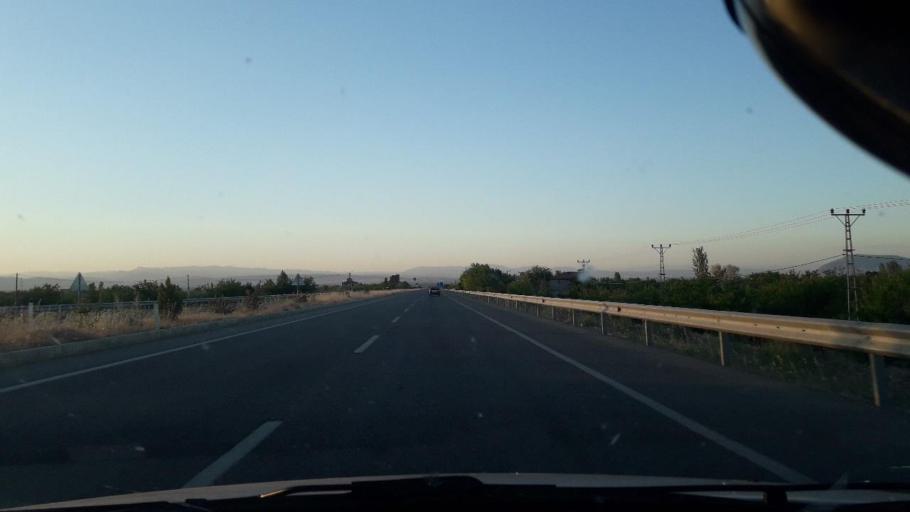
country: TR
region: Malatya
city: Malatya
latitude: 38.4377
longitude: 38.2252
